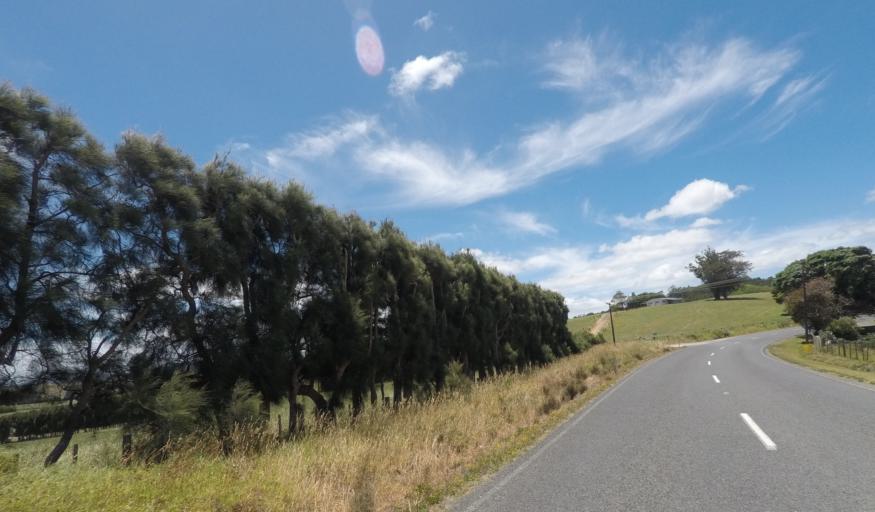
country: NZ
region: Northland
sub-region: Whangarei
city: Whangarei
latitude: -35.5598
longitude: 174.2876
